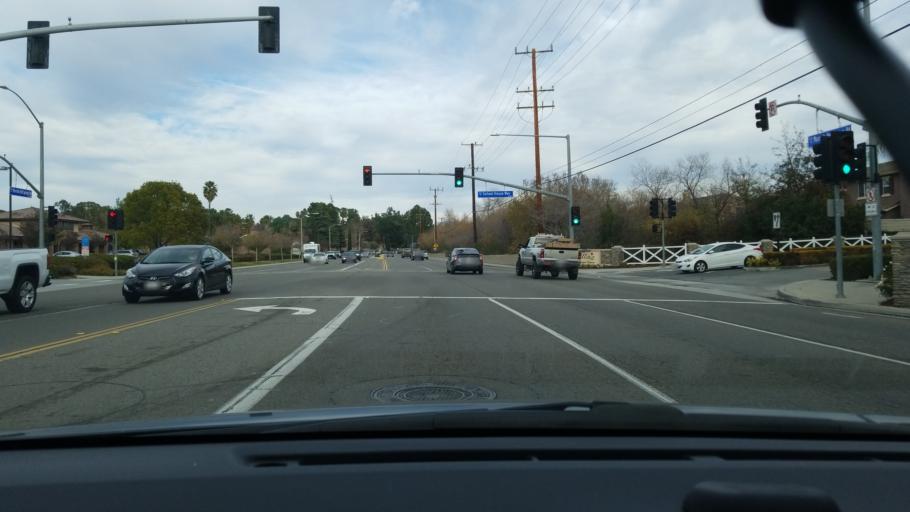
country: US
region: California
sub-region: Riverside County
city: Murrieta Hot Springs
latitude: 33.5550
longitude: -117.1638
